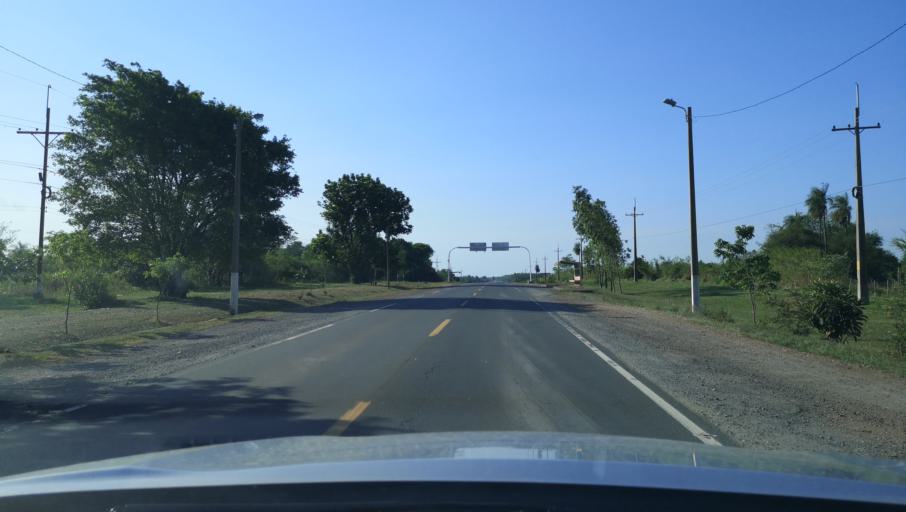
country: PY
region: Misiones
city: Santa Maria
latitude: -26.7832
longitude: -57.0269
